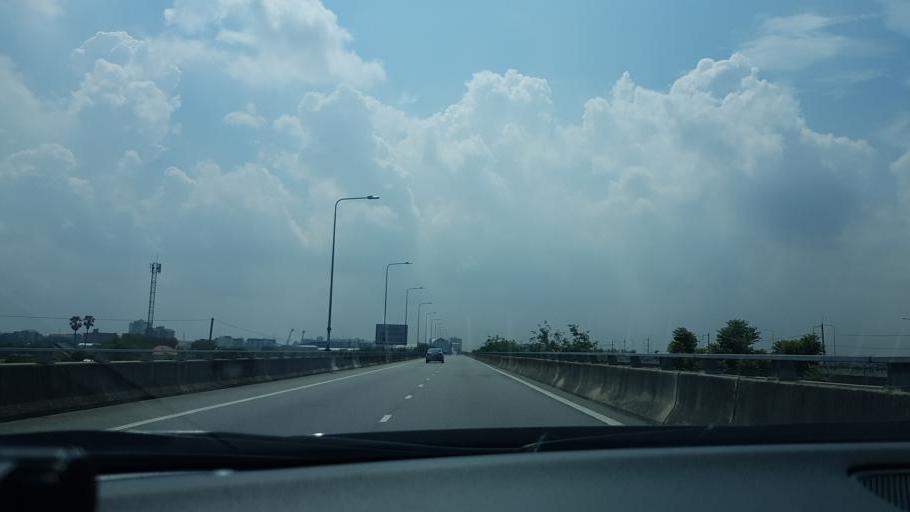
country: TH
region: Pathum Thani
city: Khlong Luang
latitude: 14.0662
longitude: 100.5859
